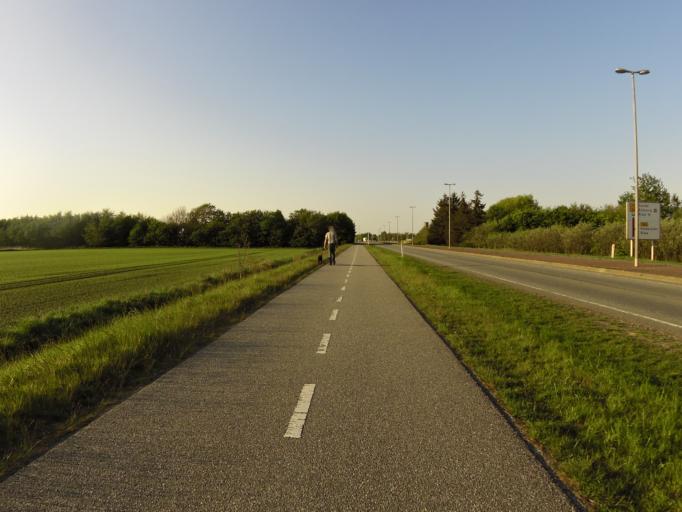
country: DK
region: South Denmark
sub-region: Esbjerg Kommune
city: Ribe
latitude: 55.3176
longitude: 8.7523
